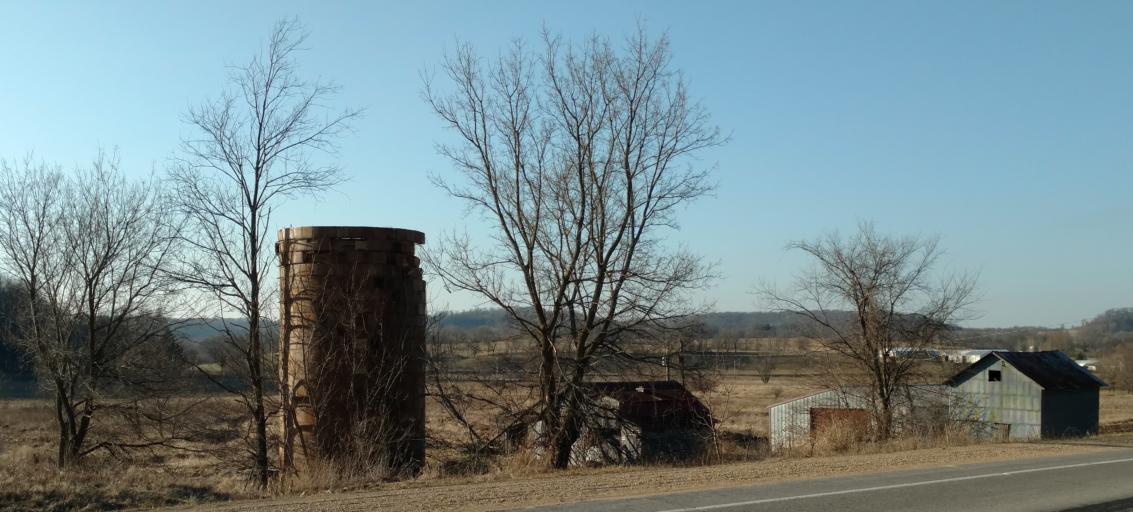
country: US
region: Wisconsin
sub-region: Vernon County
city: Hillsboro
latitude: 43.6228
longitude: -90.3585
